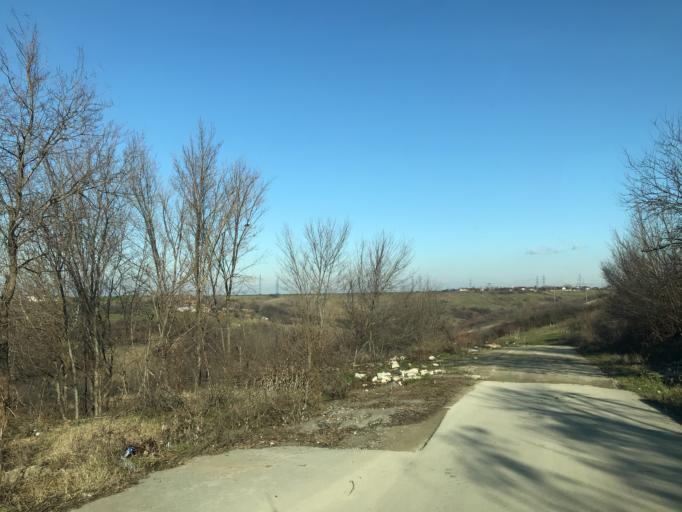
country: RO
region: Olt
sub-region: Municipiul Slatina
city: Slatina
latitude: 44.4567
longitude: 24.3738
